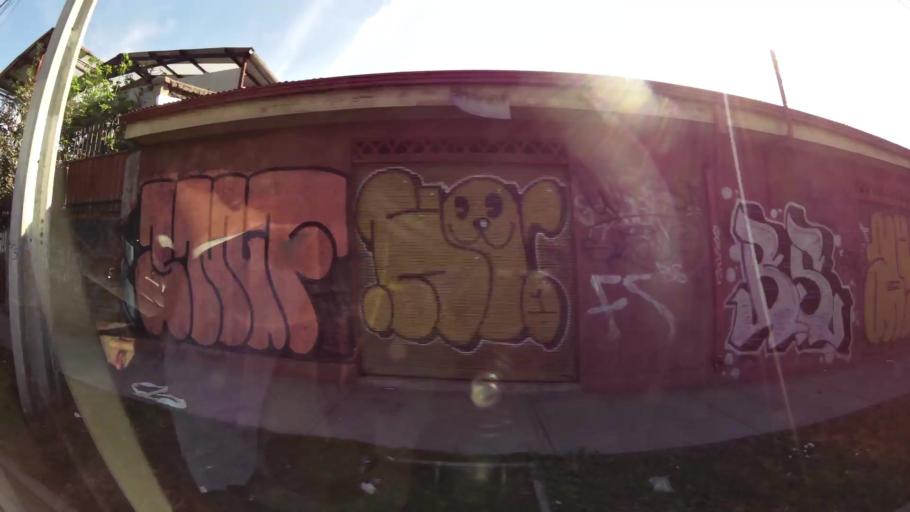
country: CL
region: Santiago Metropolitan
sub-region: Provincia de Santiago
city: Santiago
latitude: -33.4977
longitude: -70.6284
